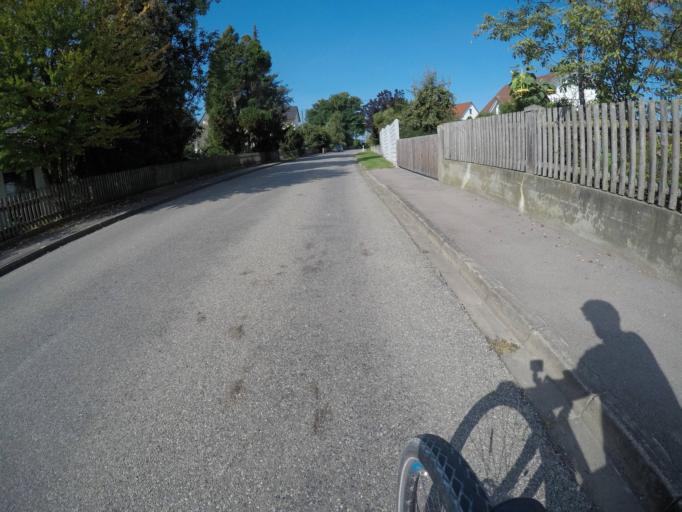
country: DE
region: Bavaria
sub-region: Swabia
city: Allmannshofen
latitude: 48.6208
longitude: 10.7674
